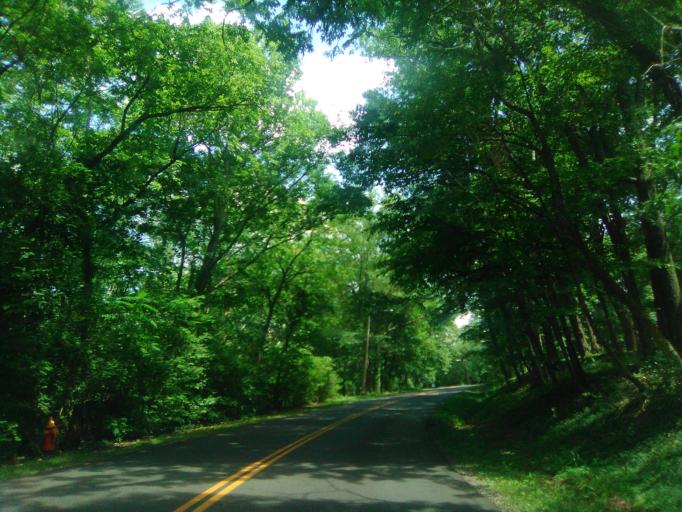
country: US
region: Tennessee
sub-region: Davidson County
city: Belle Meade
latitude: 36.1284
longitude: -86.8728
